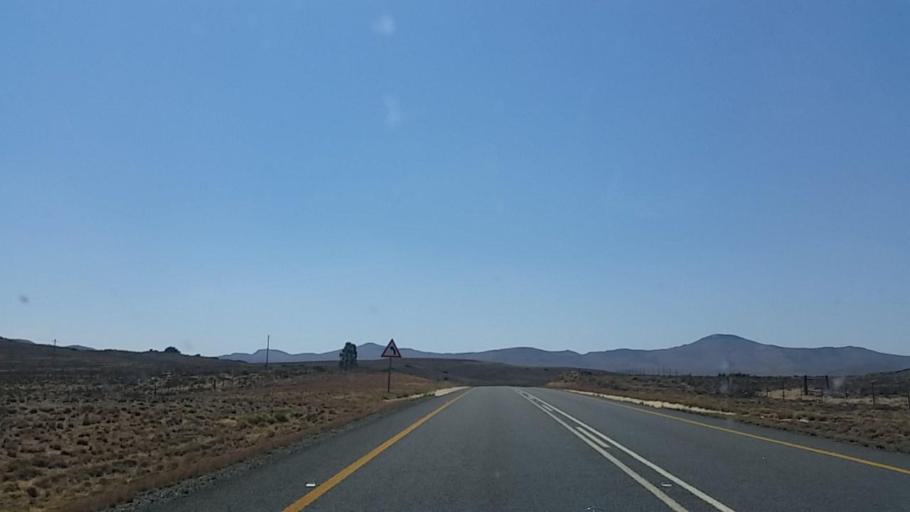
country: ZA
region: Eastern Cape
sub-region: Chris Hani District Municipality
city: Middelburg
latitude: -31.8835
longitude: 24.8167
